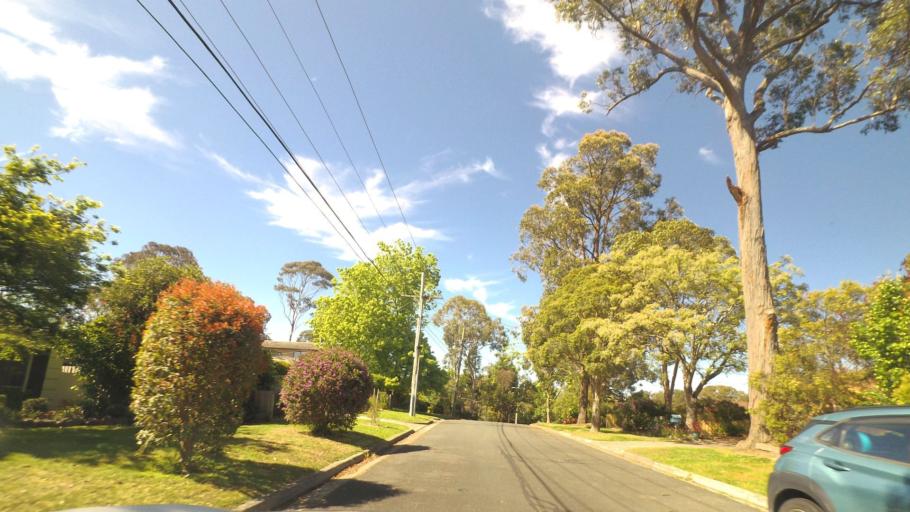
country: AU
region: Victoria
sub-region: Maroondah
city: Ringwood East
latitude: -37.8173
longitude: 145.2573
